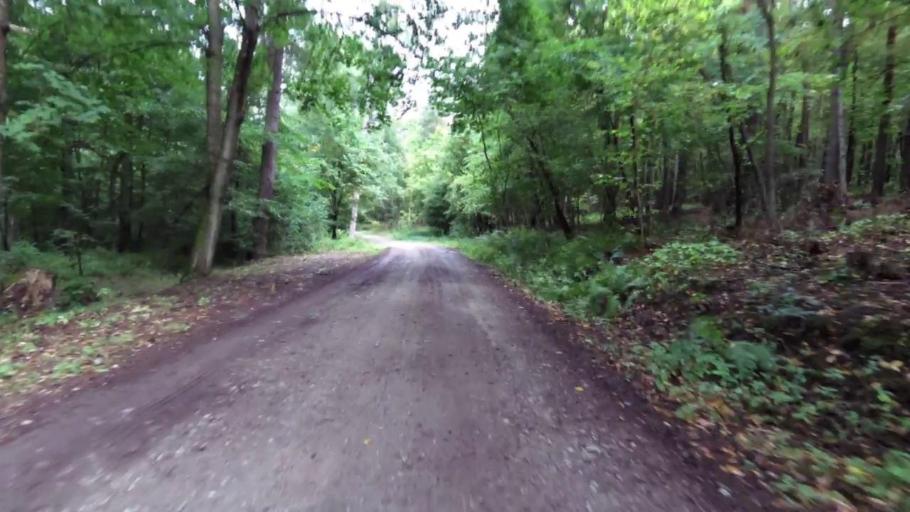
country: PL
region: West Pomeranian Voivodeship
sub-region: Powiat mysliborski
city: Debno
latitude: 52.8544
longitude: 14.6996
